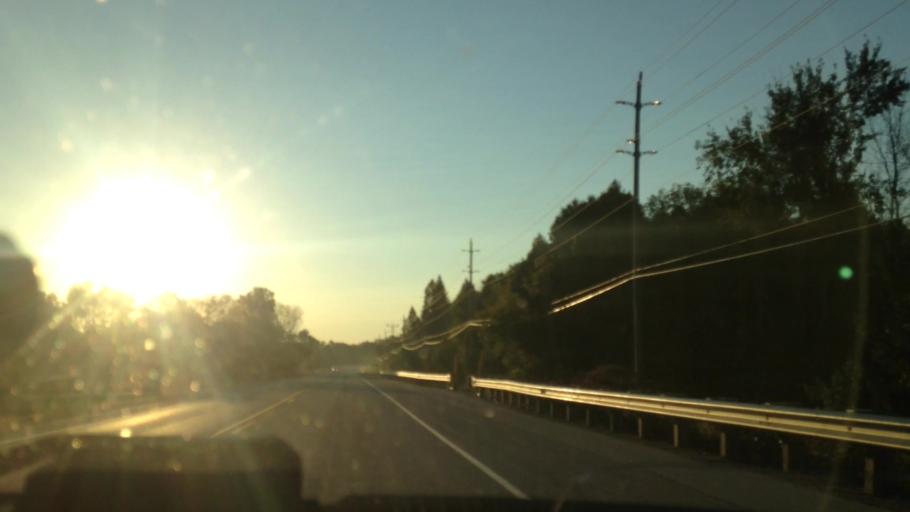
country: US
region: Wisconsin
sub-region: Washington County
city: Newburg
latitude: 43.4080
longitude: -88.0004
